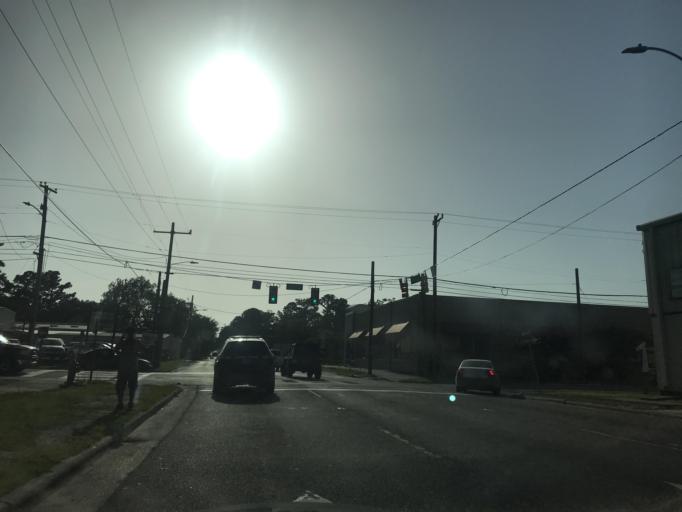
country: US
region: North Carolina
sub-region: New Hanover County
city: Wilmington
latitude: 34.2269
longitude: -77.9260
